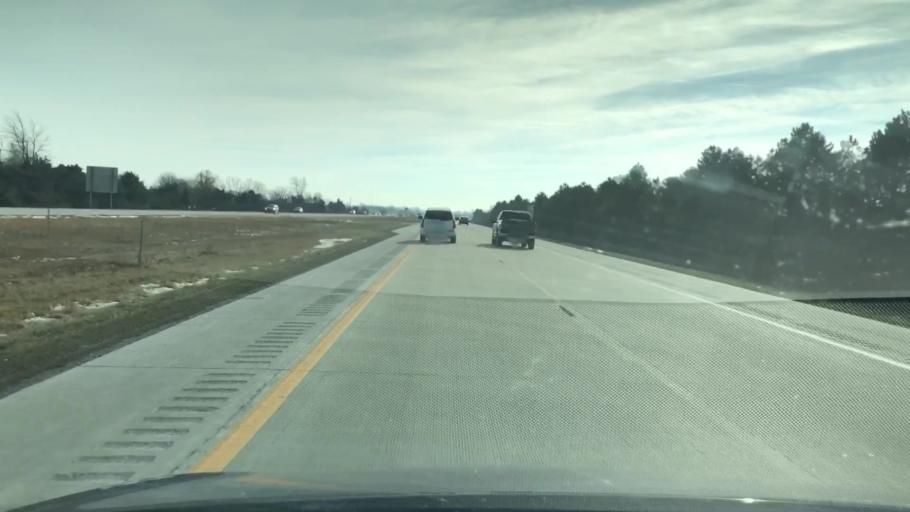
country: US
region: Michigan
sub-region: Bay County
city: Pinconning
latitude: 43.7292
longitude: -84.0147
